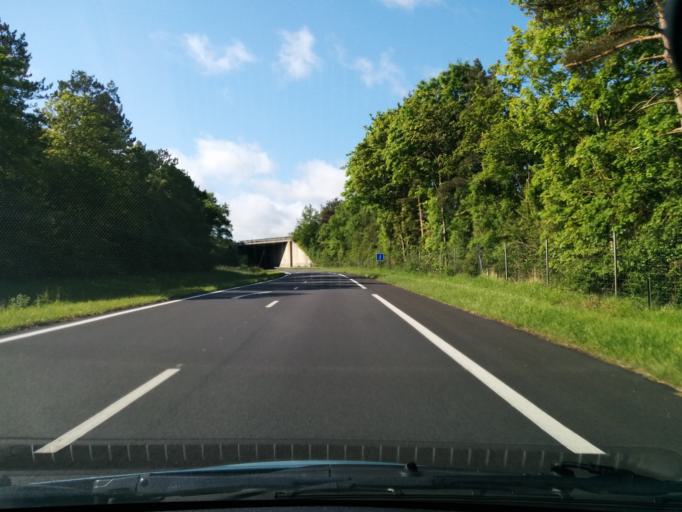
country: FR
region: Ile-de-France
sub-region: Departement des Yvelines
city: Bonnieres-sur-Seine
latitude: 49.0183
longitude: 1.5866
